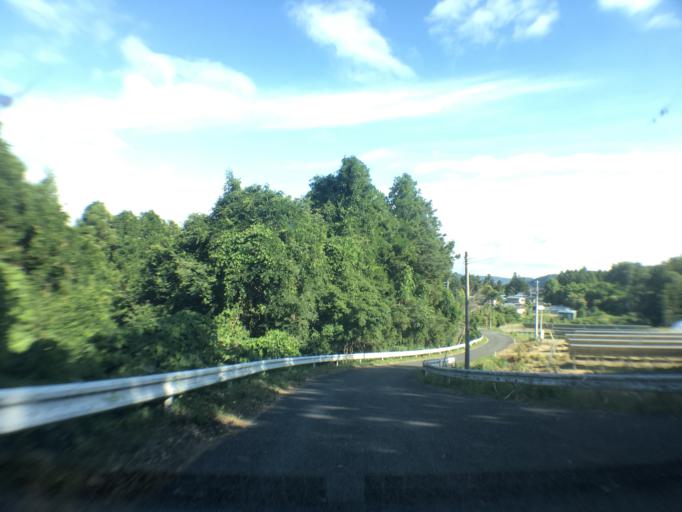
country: JP
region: Miyagi
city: Wakuya
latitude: 38.6602
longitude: 141.2820
